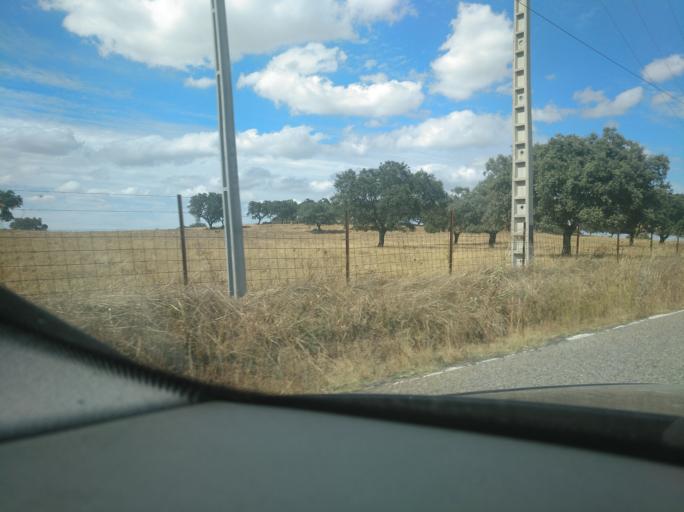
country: PT
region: Portalegre
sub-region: Arronches
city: Arronches
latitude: 39.0759
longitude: -7.3690
